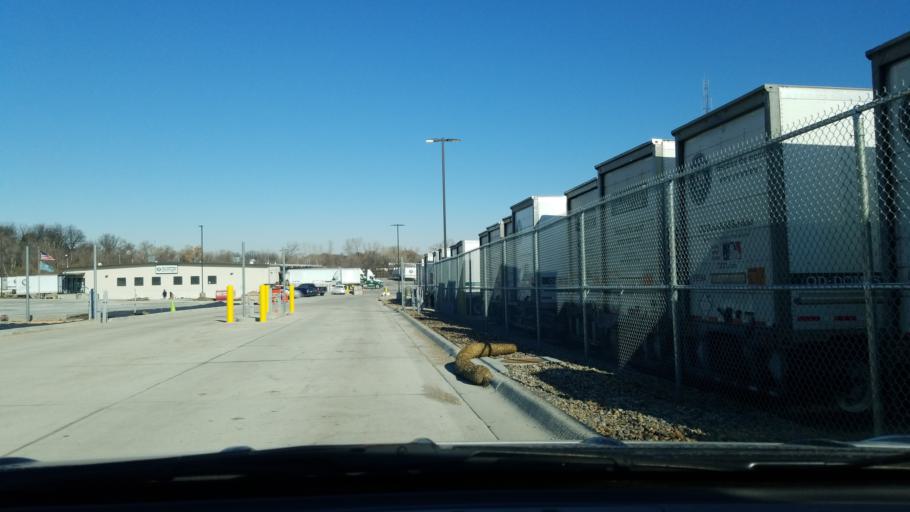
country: US
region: Nebraska
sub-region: Douglas County
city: Ralston
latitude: 41.2166
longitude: -96.0788
